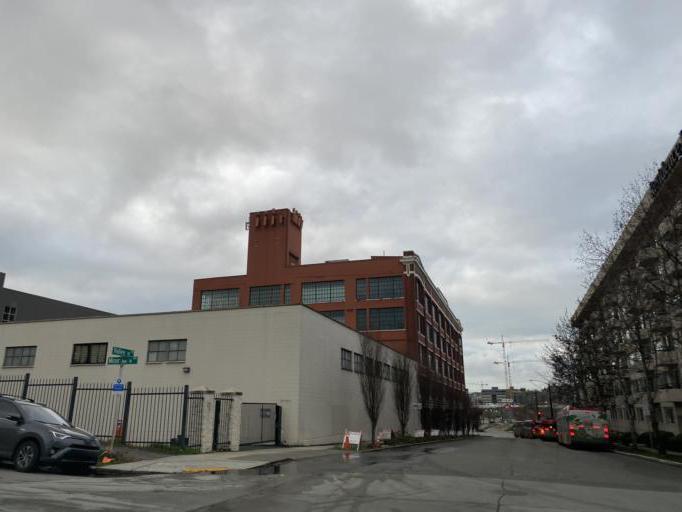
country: US
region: Washington
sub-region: King County
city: Seattle
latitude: 47.6261
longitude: -122.3325
